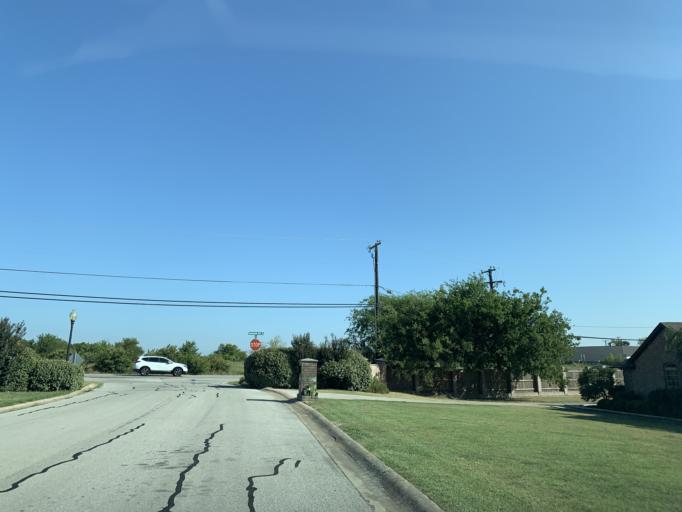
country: US
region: Texas
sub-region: Tarrant County
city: Lakeside
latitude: 32.8249
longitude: -97.4818
